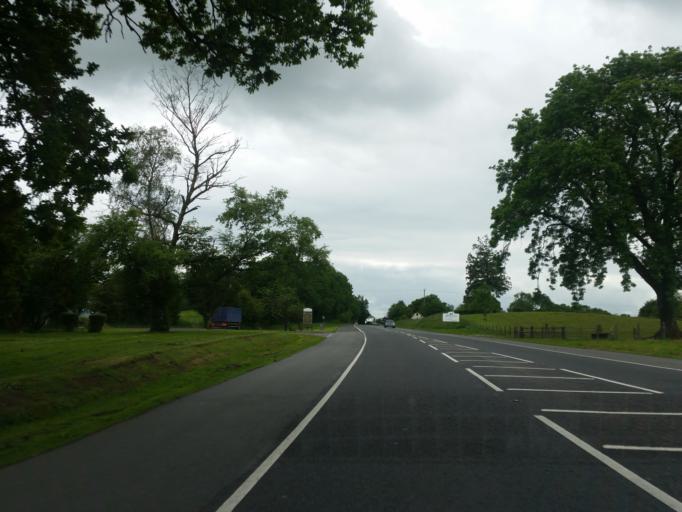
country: GB
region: Northern Ireland
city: Fivemiletown
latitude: 54.3701
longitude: -7.3347
